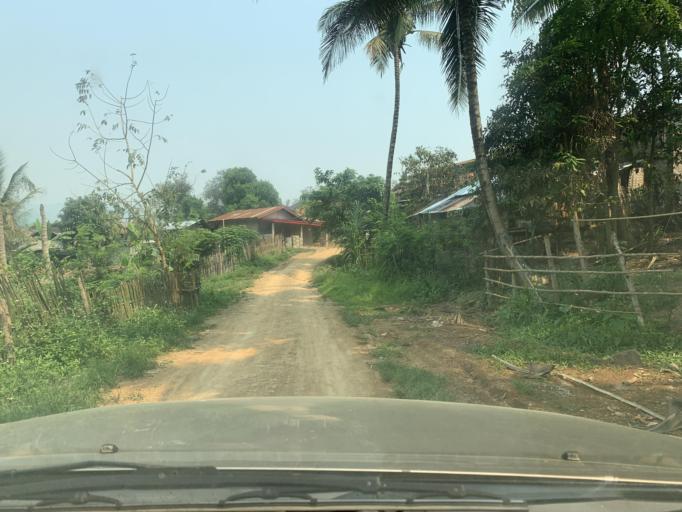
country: LA
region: Louangphabang
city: Xiang Ngeun
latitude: 19.8018
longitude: 102.2044
